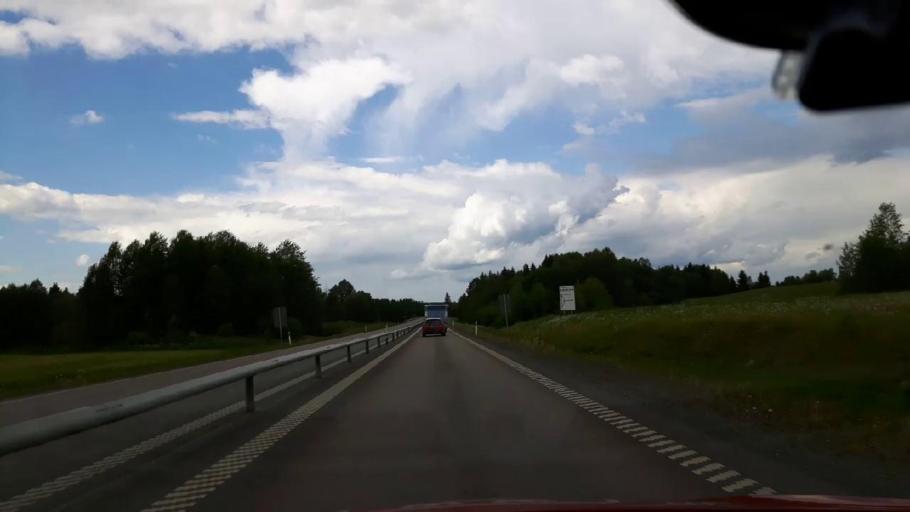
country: SE
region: Jaemtland
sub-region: Krokoms Kommun
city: Krokom
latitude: 63.3114
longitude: 14.4751
